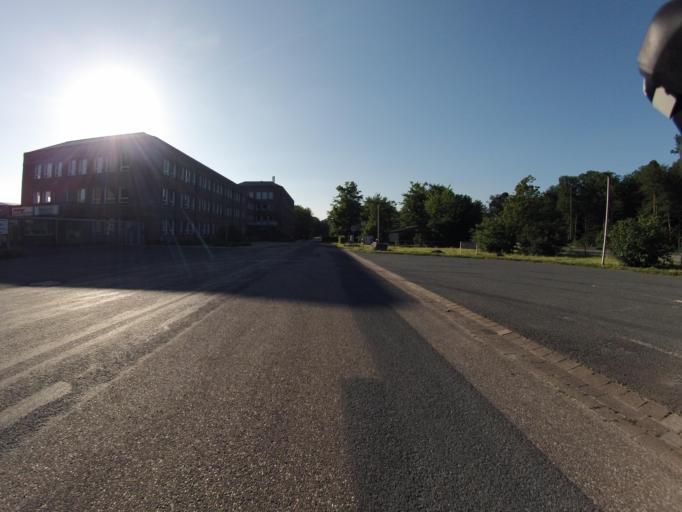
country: DE
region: Lower Saxony
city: Bad Bentheim
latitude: 52.3120
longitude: 7.1392
